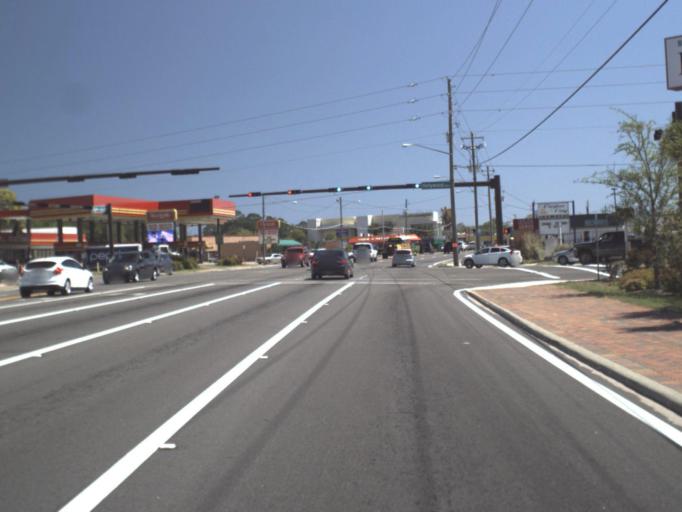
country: US
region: Florida
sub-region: Okaloosa County
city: Fort Walton Beach
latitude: 30.4128
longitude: -86.6047
